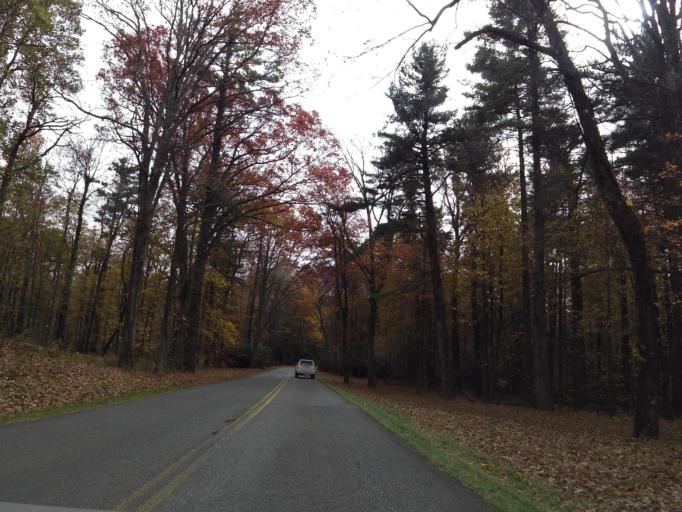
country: US
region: Virginia
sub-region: Carroll County
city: Cana
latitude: 36.6109
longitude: -80.7808
